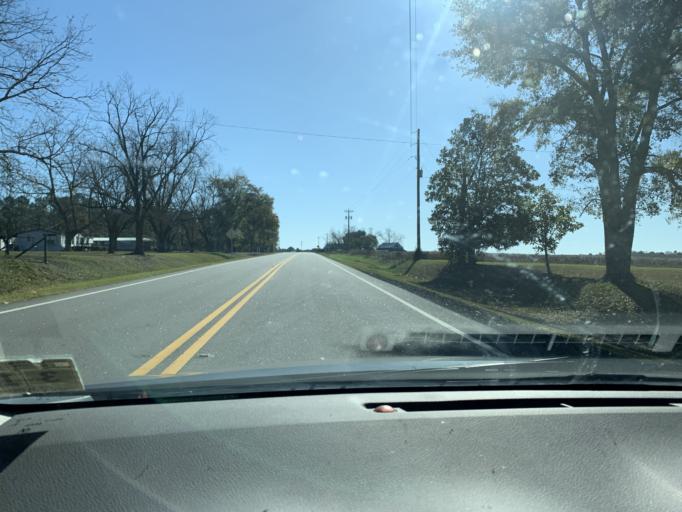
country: US
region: Georgia
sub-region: Ben Hill County
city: Fitzgerald
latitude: 31.7114
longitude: -83.1687
